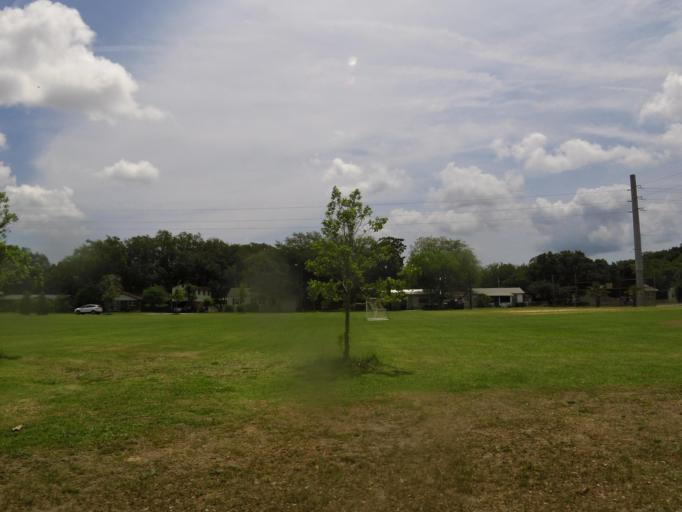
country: US
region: Florida
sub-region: Nassau County
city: Fernandina Beach
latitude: 30.6621
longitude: -81.4584
